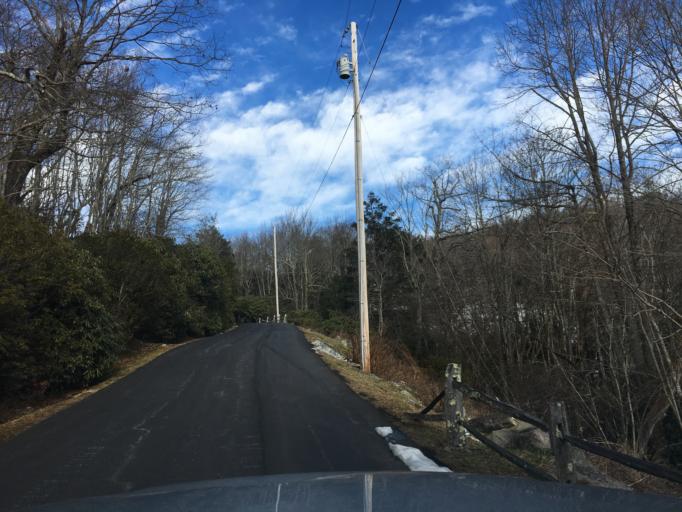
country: US
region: North Carolina
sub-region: Jackson County
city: Cullowhee
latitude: 35.1350
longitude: -82.9978
